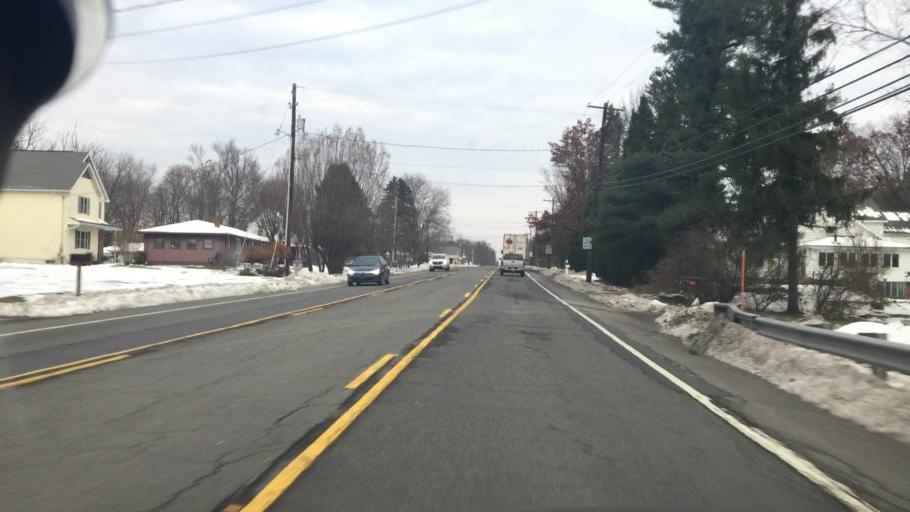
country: US
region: Pennsylvania
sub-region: Luzerne County
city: Mountain Top
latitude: 41.1254
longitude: -75.9077
